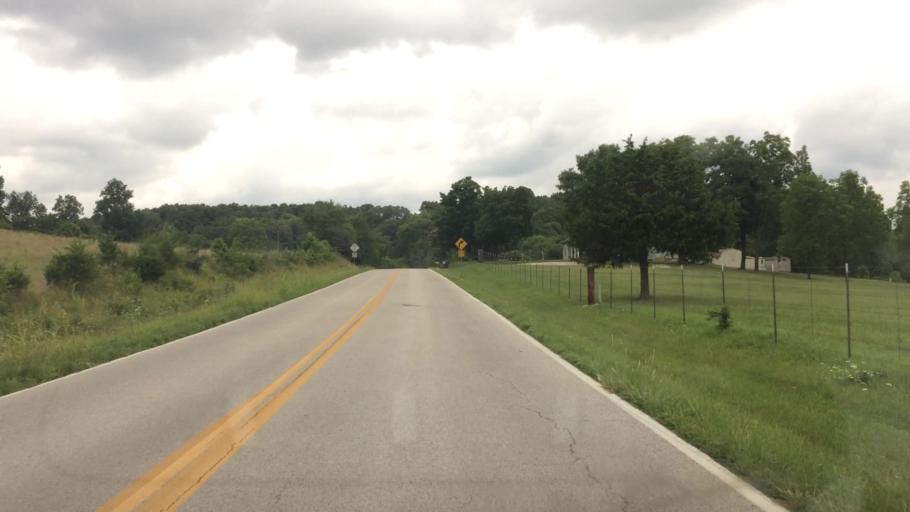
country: US
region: Missouri
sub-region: Greene County
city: Strafford
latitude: 37.2943
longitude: -93.0855
